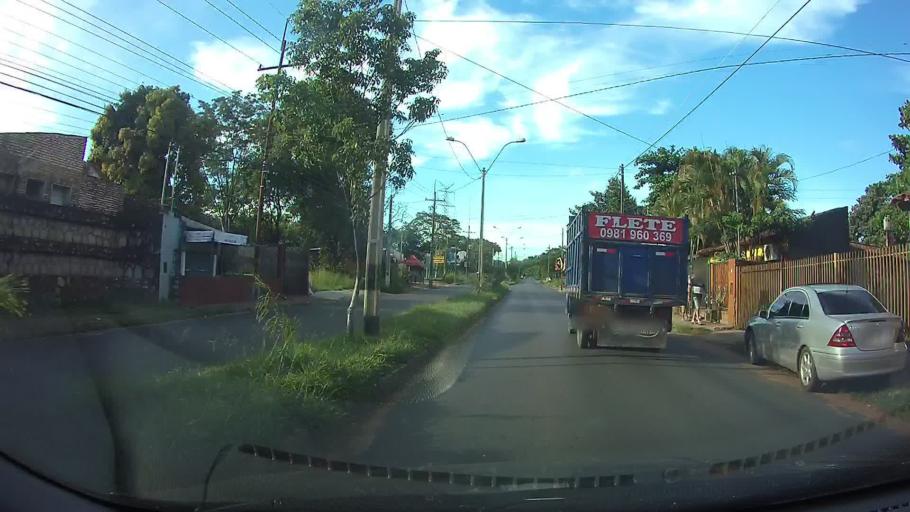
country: PY
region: Central
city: Villa Elisa
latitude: -25.3903
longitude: -57.5826
